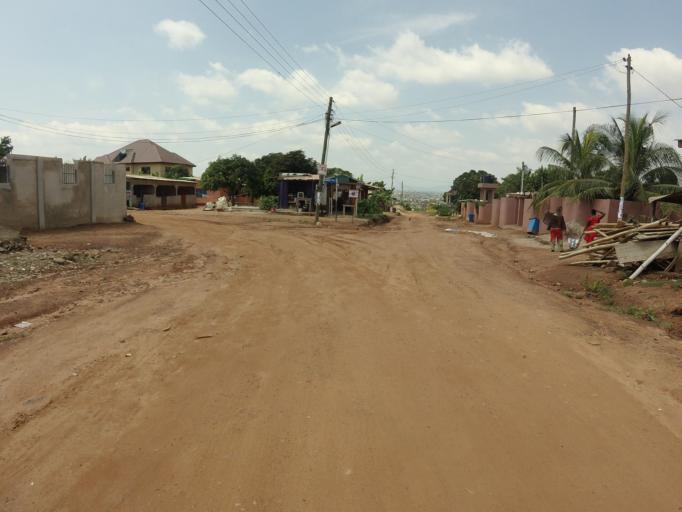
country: GH
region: Greater Accra
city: Gbawe
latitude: 5.6184
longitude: -0.3107
